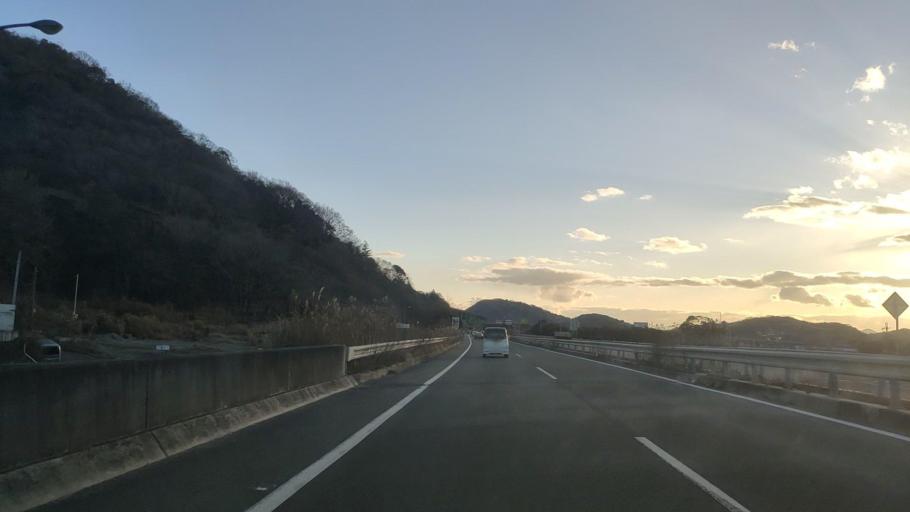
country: JP
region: Hyogo
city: Tatsunocho-tominaga
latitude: 34.8522
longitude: 134.6052
